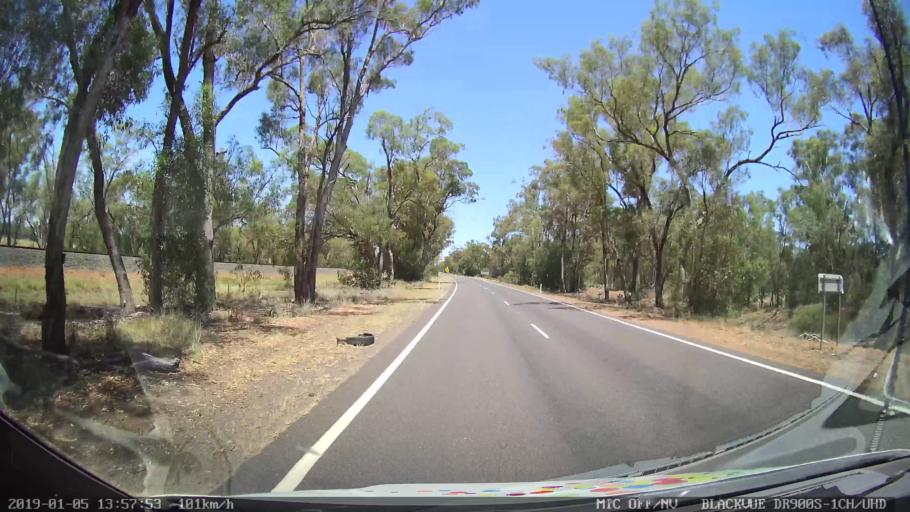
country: AU
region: New South Wales
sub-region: Gunnedah
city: Gunnedah
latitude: -31.1328
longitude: 150.2779
